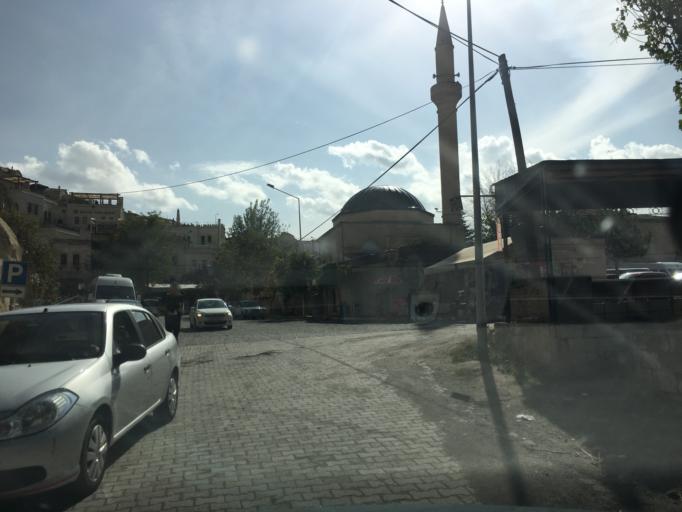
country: TR
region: Nevsehir
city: Goereme
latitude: 38.6676
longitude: 34.8420
